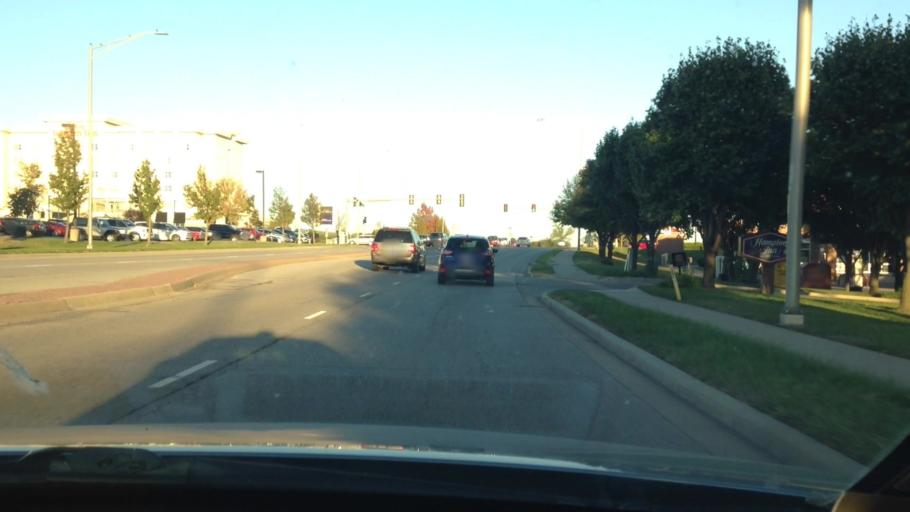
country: US
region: Kansas
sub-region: Johnson County
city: Olathe
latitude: 38.9099
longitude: -94.7720
